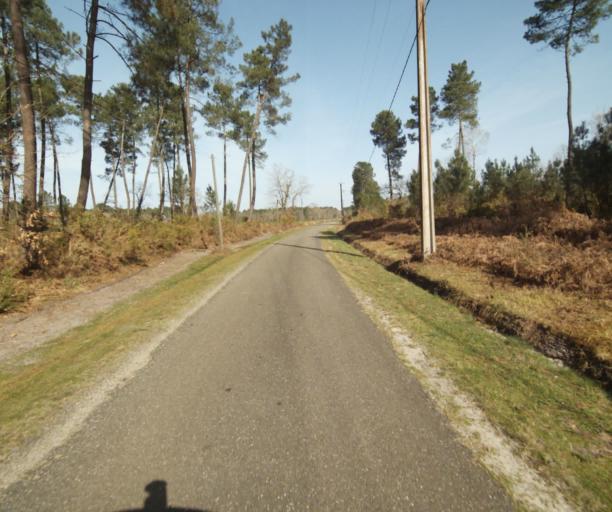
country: FR
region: Aquitaine
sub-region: Departement des Landes
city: Roquefort
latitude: 44.1432
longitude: -0.2401
